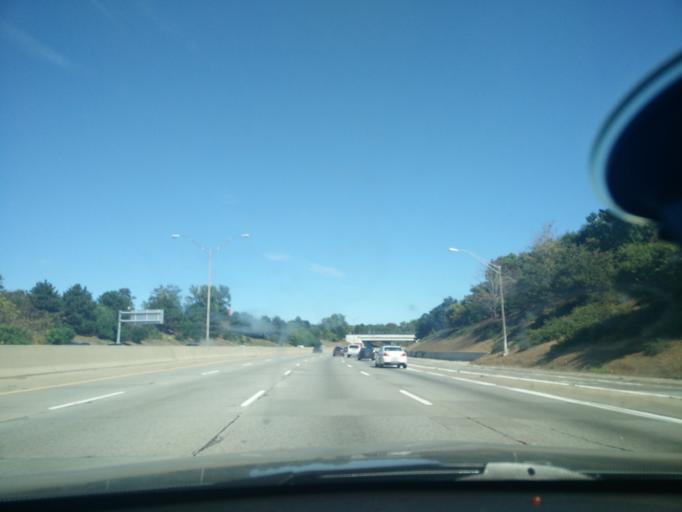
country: US
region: Michigan
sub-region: Oakland County
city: Madison Heights
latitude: 42.4878
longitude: -83.0818
